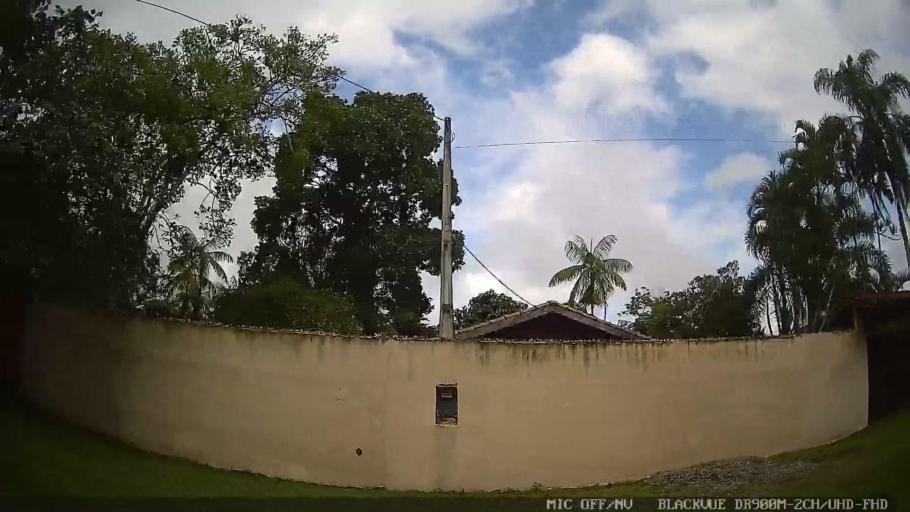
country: BR
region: Sao Paulo
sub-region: Itanhaem
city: Itanhaem
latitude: -24.2109
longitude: -46.8900
